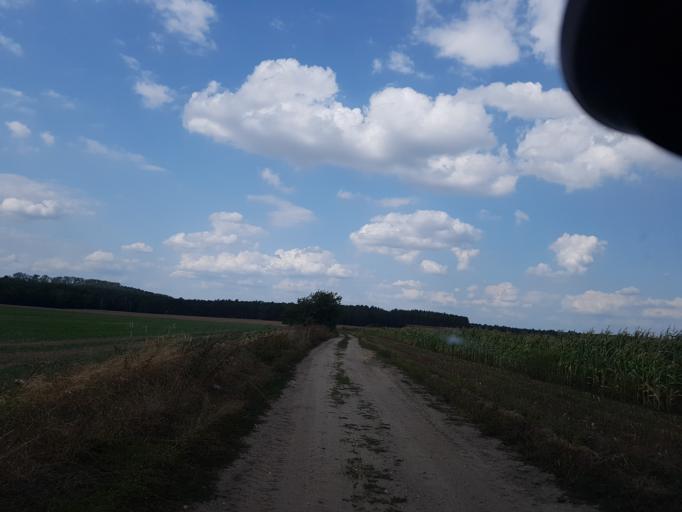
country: DE
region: Brandenburg
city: Calau
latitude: 51.7563
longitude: 13.9515
